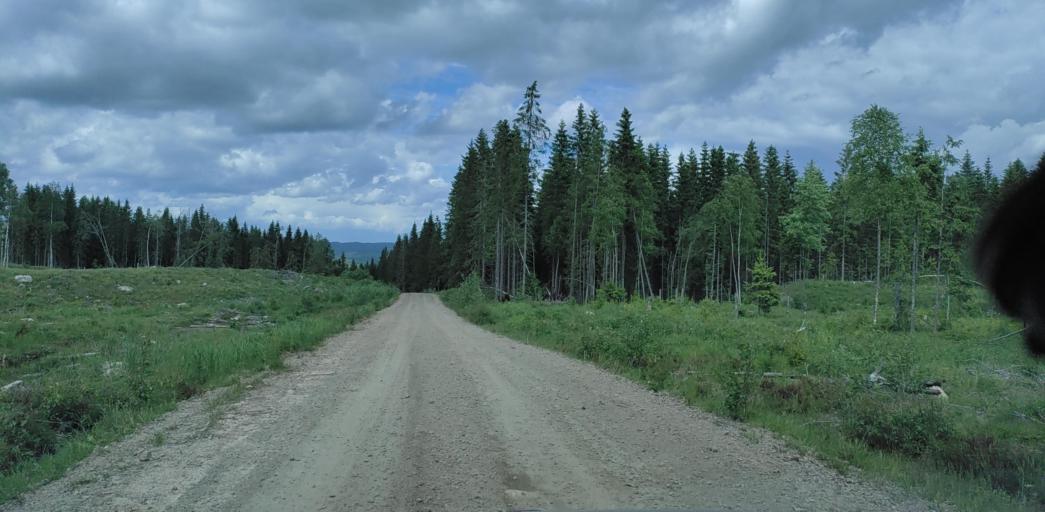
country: SE
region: Vaermland
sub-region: Munkfors Kommun
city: Munkfors
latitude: 59.9575
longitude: 13.4125
